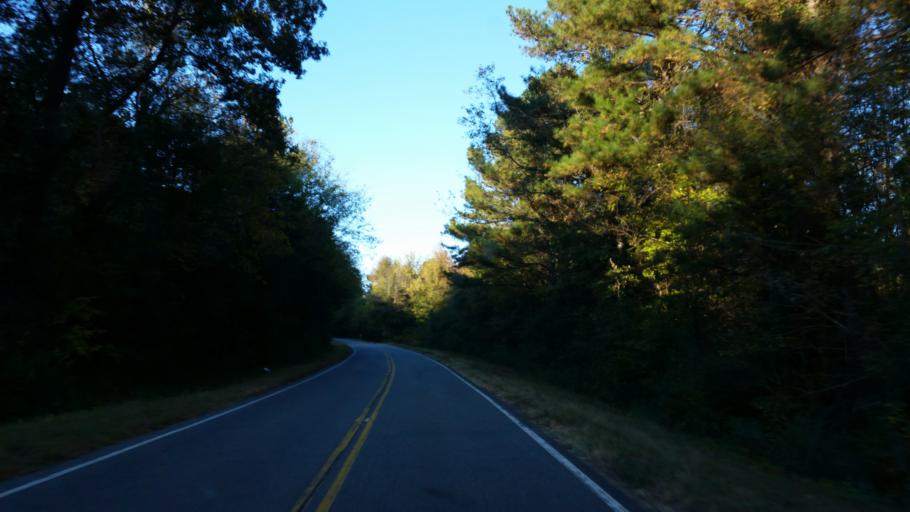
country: US
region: Georgia
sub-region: Bartow County
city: Adairsville
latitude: 34.2955
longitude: -84.9411
